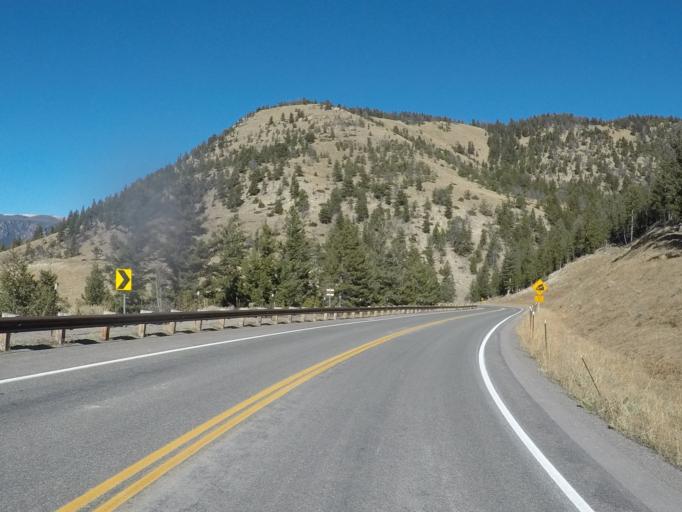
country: US
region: Wyoming
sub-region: Park County
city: Cody
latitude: 44.7513
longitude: -109.3986
